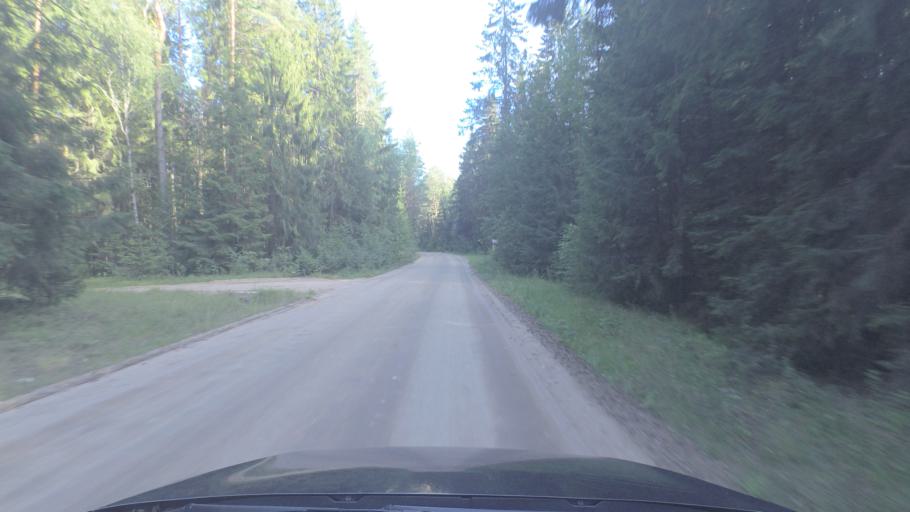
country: LT
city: Svencioneliai
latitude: 55.1653
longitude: 25.8416
